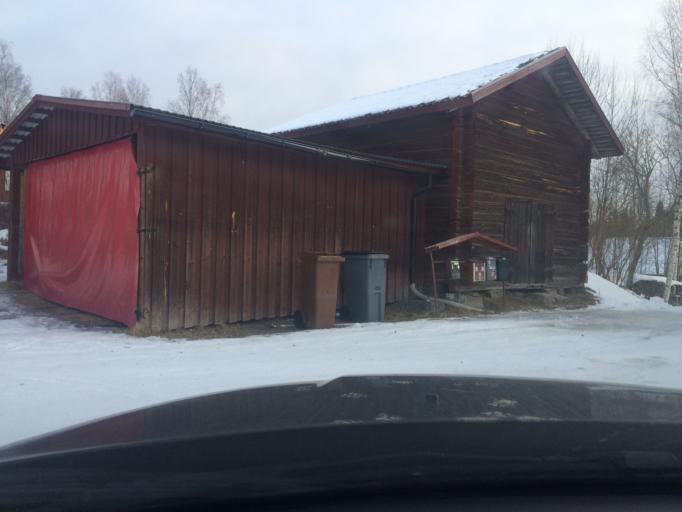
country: SE
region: Dalarna
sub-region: Gagnefs Kommun
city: Mockfjard
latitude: 60.4948
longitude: 14.8497
